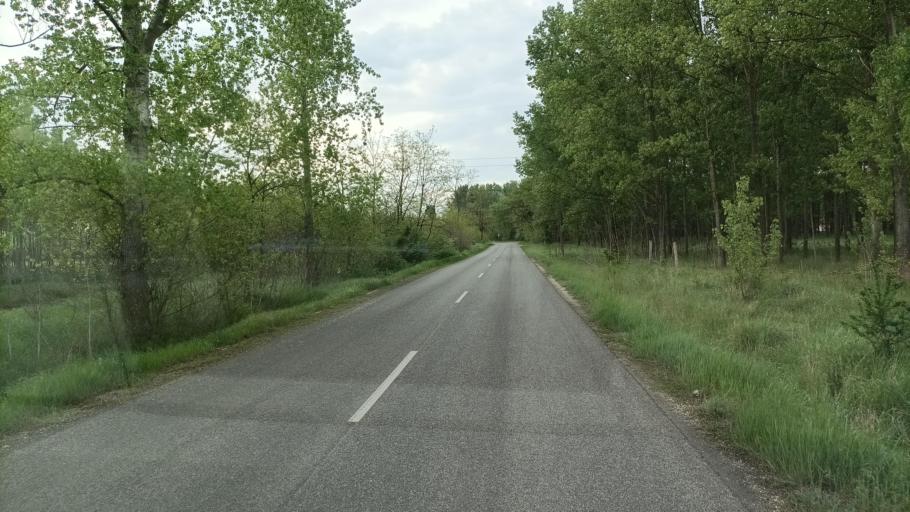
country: HU
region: Pest
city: Monor
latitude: 47.3125
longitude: 19.4177
